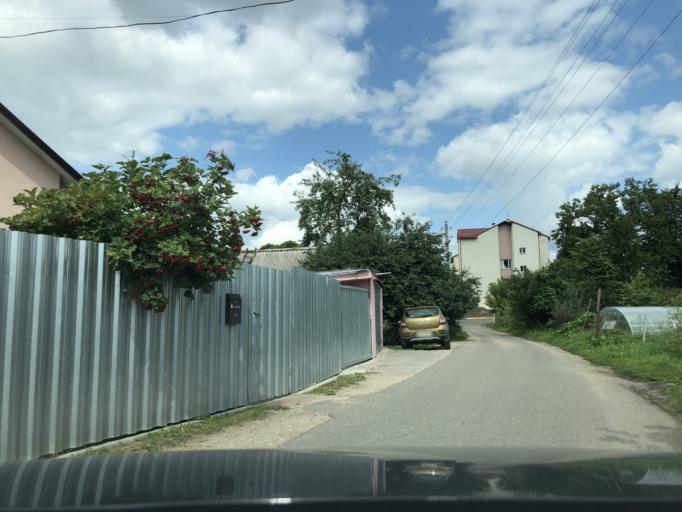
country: BY
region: Minsk
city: Lahoysk
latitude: 54.2045
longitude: 27.8519
